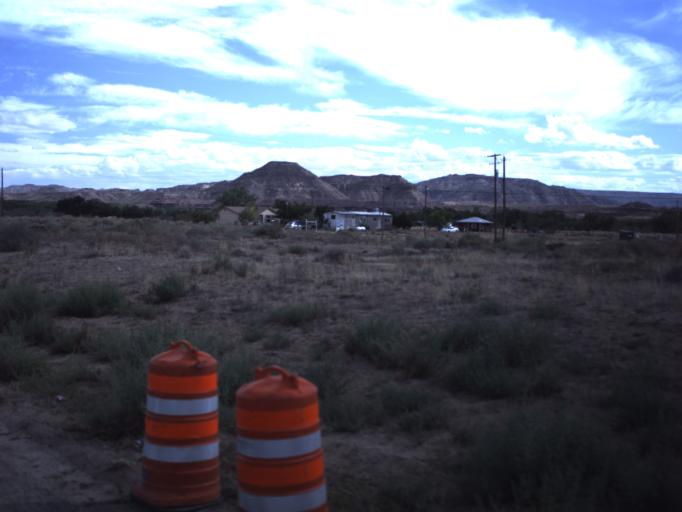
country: US
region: Utah
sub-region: San Juan County
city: Blanding
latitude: 37.2286
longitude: -109.2129
